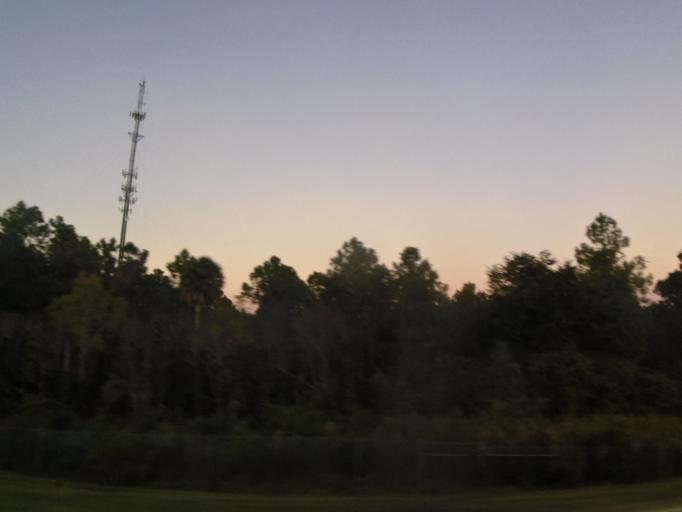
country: US
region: Florida
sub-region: Flagler County
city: Palm Coast
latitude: 29.6009
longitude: -81.2464
